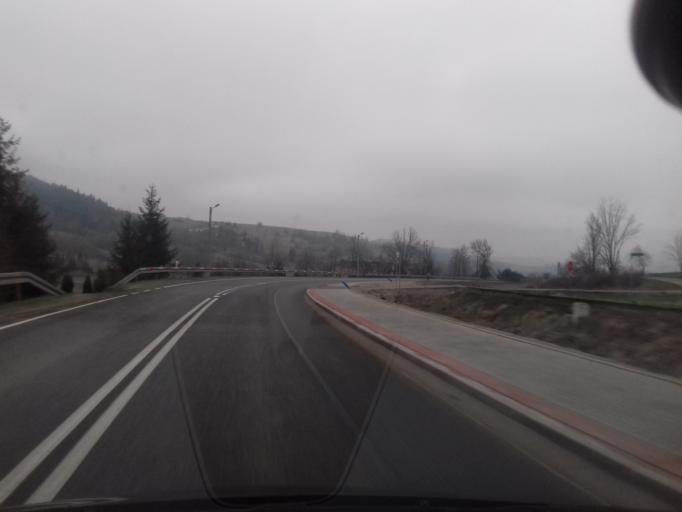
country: PL
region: Lesser Poland Voivodeship
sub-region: Powiat limanowski
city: Kasina Wielka
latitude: 49.6988
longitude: 20.1272
